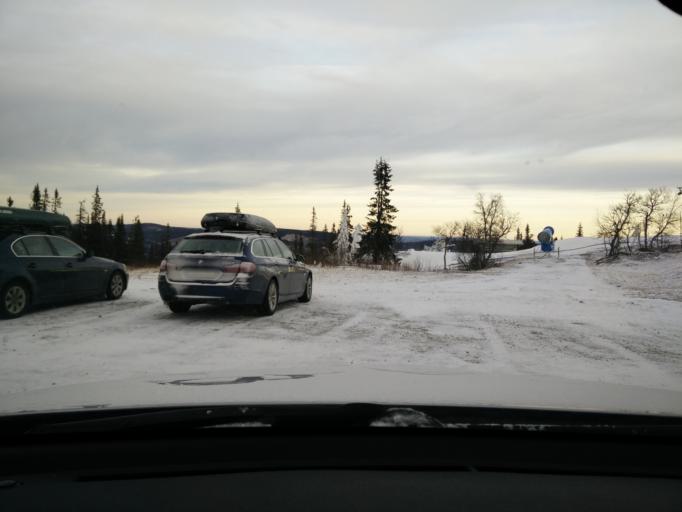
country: SE
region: Jaemtland
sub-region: Bergs Kommun
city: Hoverberg
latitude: 62.4943
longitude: 14.1580
